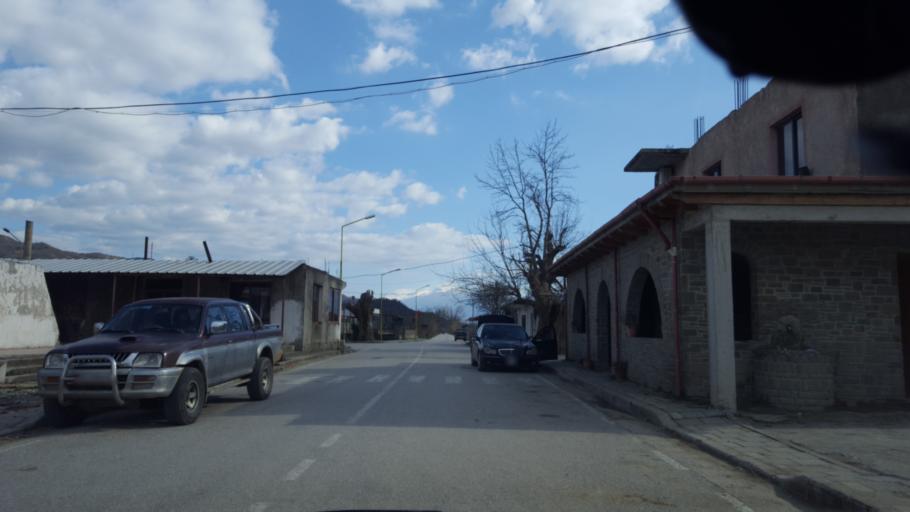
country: AL
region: Gjirokaster
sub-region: Rrethi i Permetit
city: Ballaban
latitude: 40.4144
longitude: 20.1238
